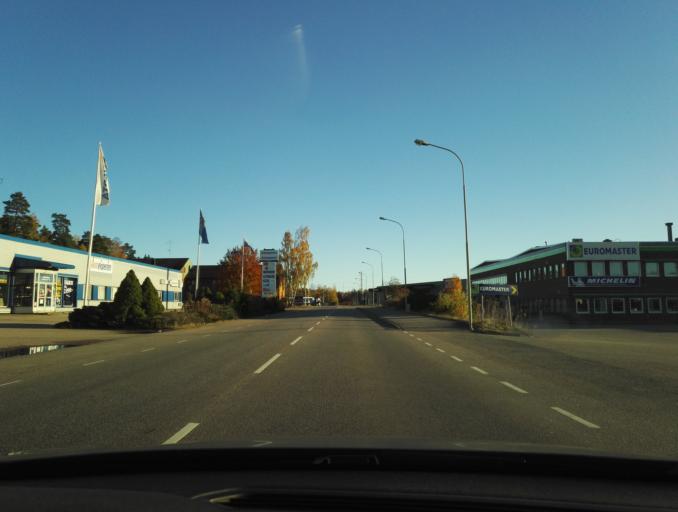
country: SE
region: Kronoberg
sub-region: Vaxjo Kommun
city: Vaexjoe
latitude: 56.8922
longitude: 14.7722
